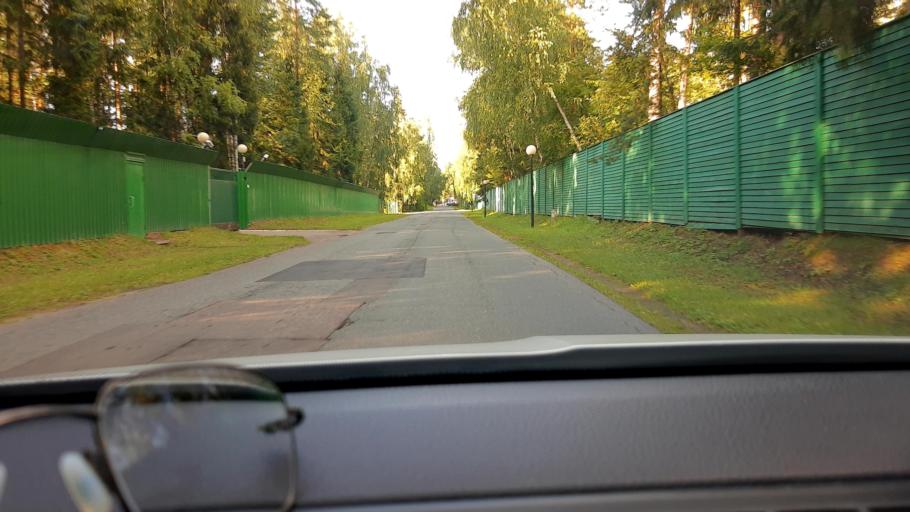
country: RU
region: Moskovskaya
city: Nikolina Gora
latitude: 55.7202
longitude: 36.9616
